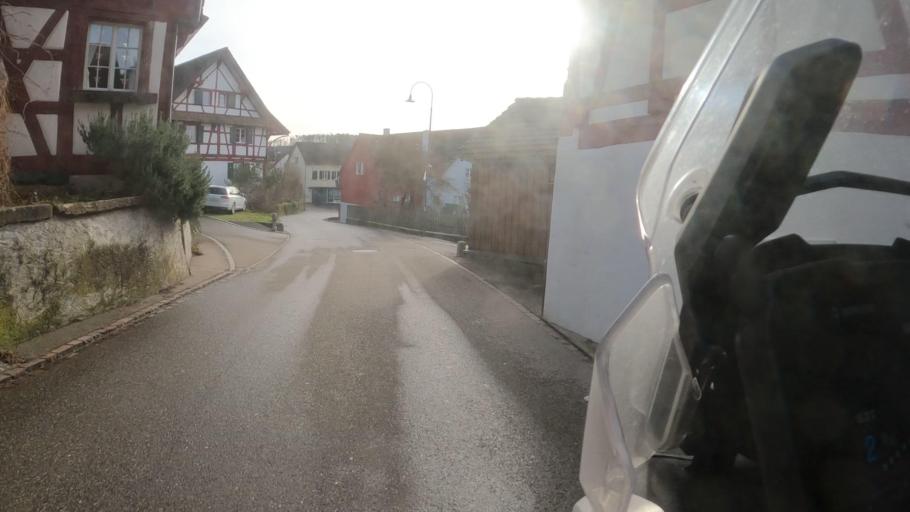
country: CH
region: Zurich
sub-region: Bezirk Buelach
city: Glattfelden
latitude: 47.5596
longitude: 8.4995
